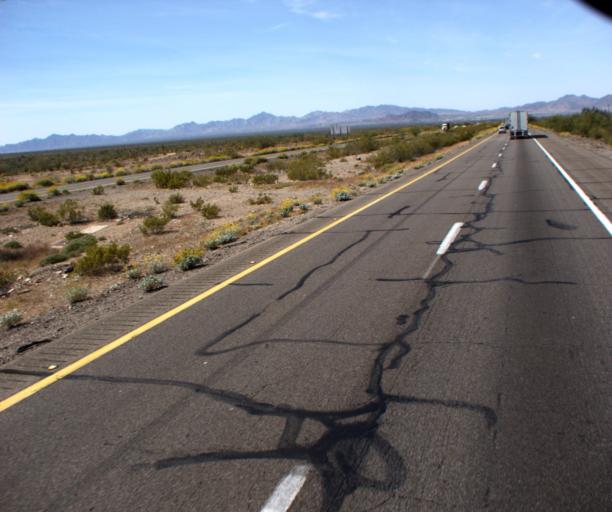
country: US
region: Arizona
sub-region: La Paz County
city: Quartzsite
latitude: 33.6789
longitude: -114.1030
